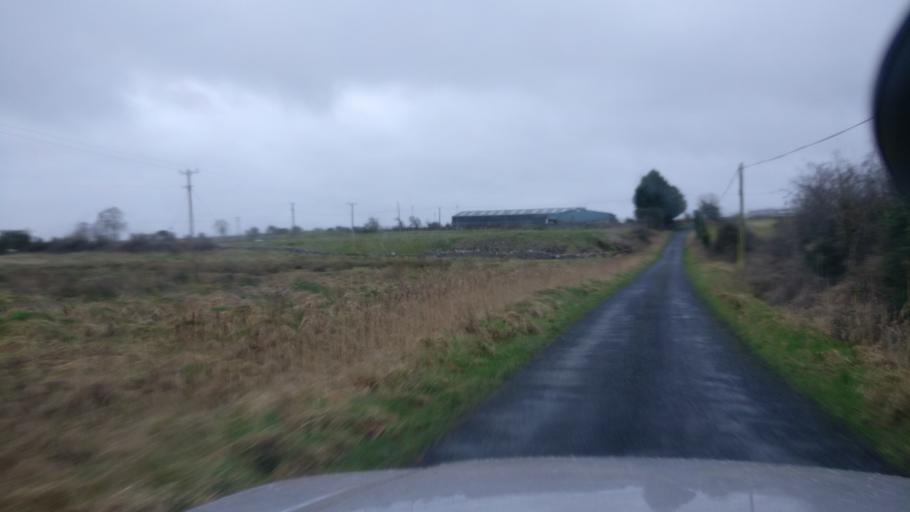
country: IE
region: Connaught
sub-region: County Galway
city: Loughrea
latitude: 53.2108
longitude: -8.5881
